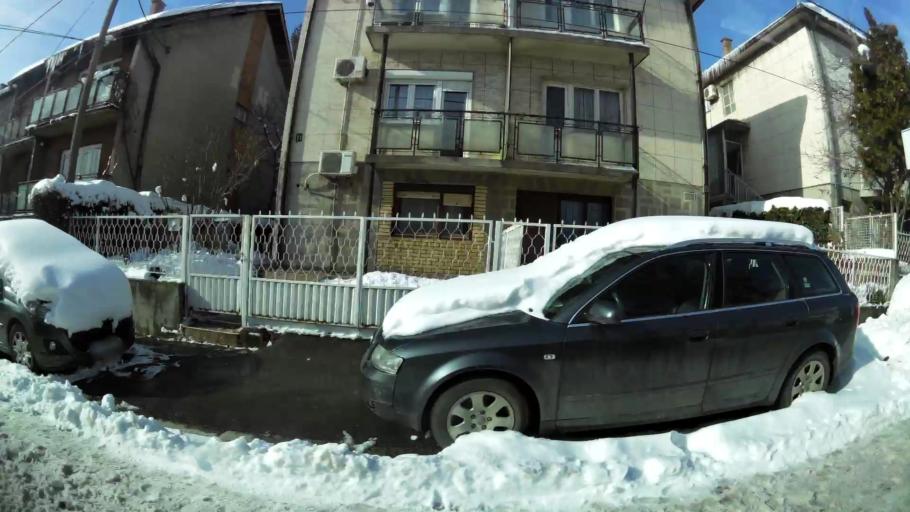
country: RS
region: Central Serbia
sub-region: Belgrade
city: Palilula
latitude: 44.7961
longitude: 20.5244
